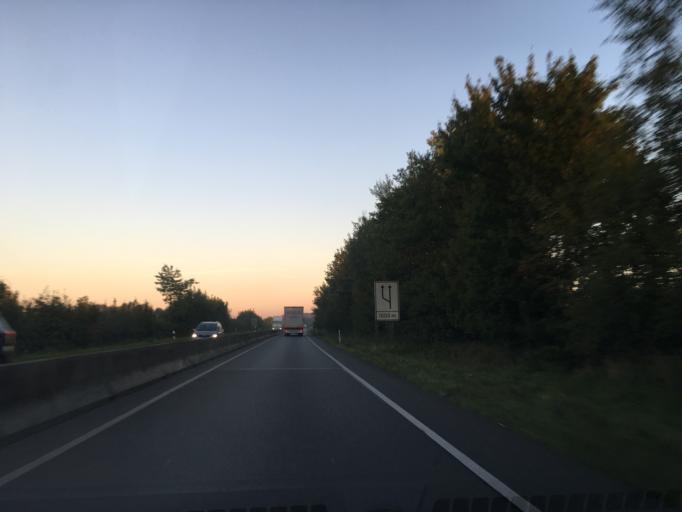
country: DE
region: North Rhine-Westphalia
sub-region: Regierungsbezirk Munster
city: Altenberge
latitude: 51.9968
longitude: 7.5284
